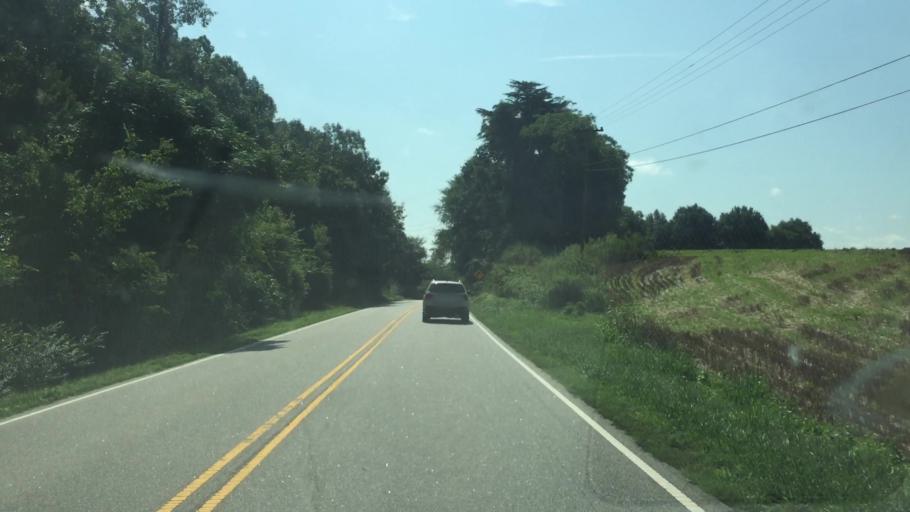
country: US
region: North Carolina
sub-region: Anson County
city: Burnsville
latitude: 35.1180
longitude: -80.3439
